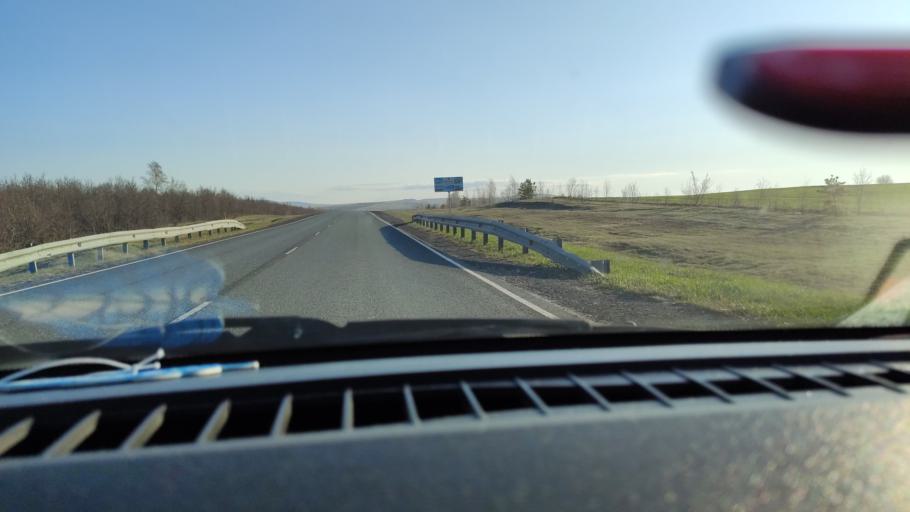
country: RU
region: Saratov
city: Balakovo
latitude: 52.1800
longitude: 47.8409
